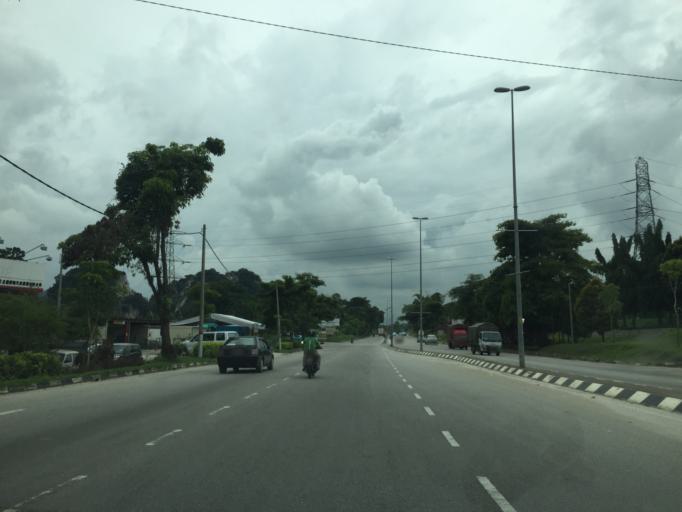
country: MY
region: Perak
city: Ipoh
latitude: 4.5527
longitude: 101.1166
